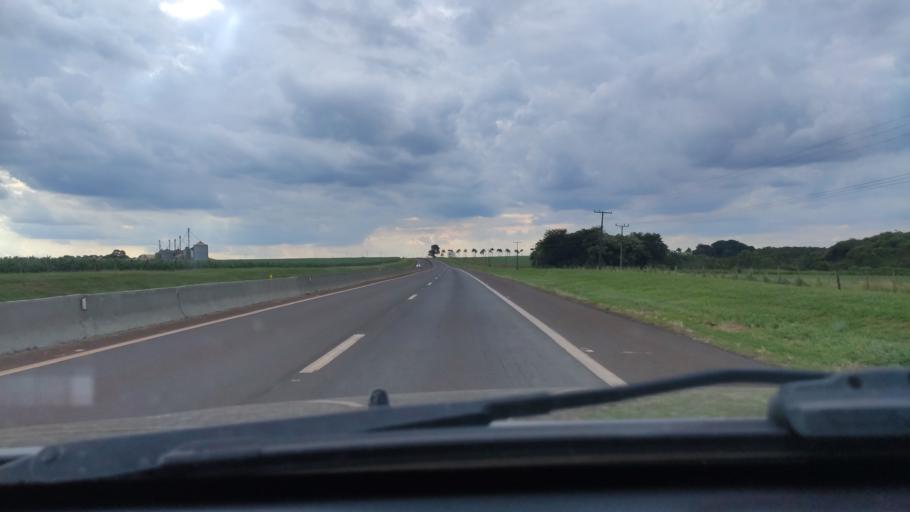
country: BR
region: Sao Paulo
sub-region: Palmital
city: Palmital
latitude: -22.8281
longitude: -50.0310
